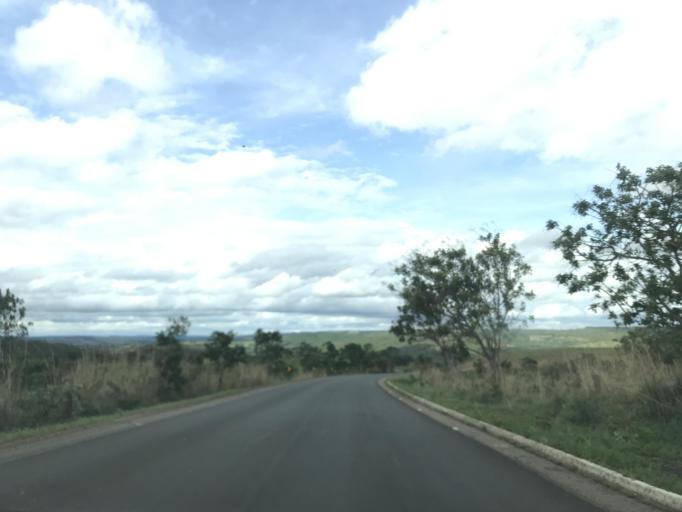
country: BR
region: Goias
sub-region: Vianopolis
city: Vianopolis
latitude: -16.9568
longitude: -48.5973
